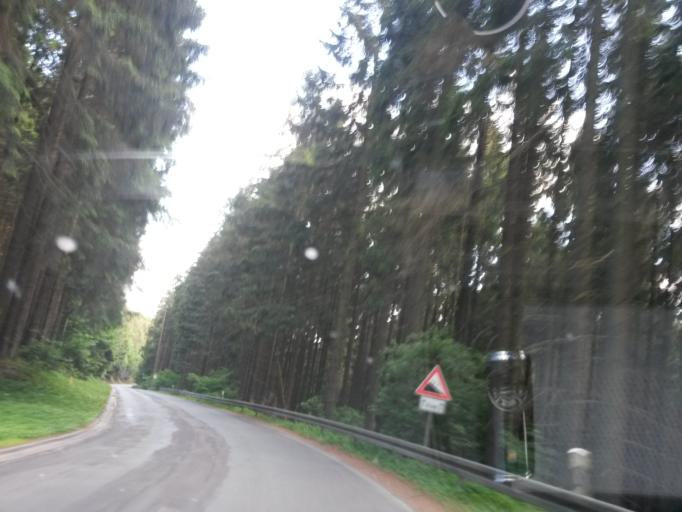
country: DE
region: North Rhine-Westphalia
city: Plettenberg
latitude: 51.2487
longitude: 7.8625
